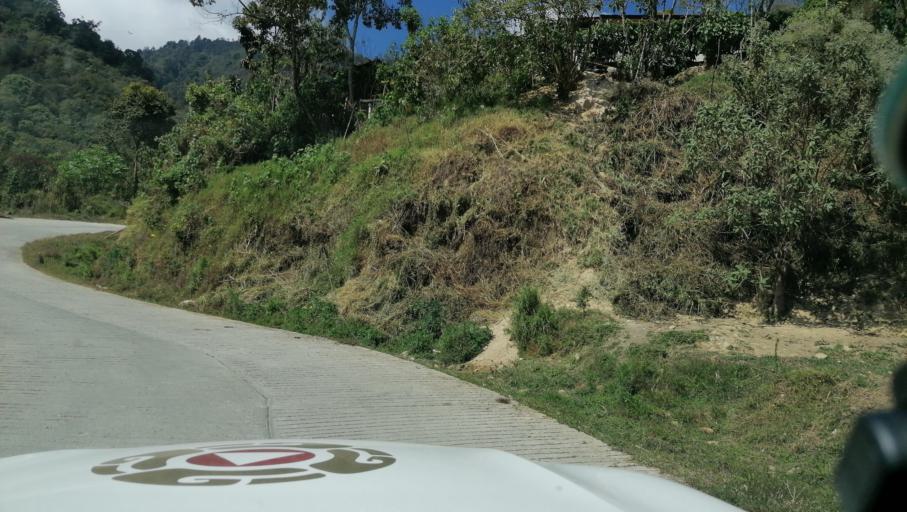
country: GT
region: San Marcos
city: Tacana
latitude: 15.2018
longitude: -92.2060
